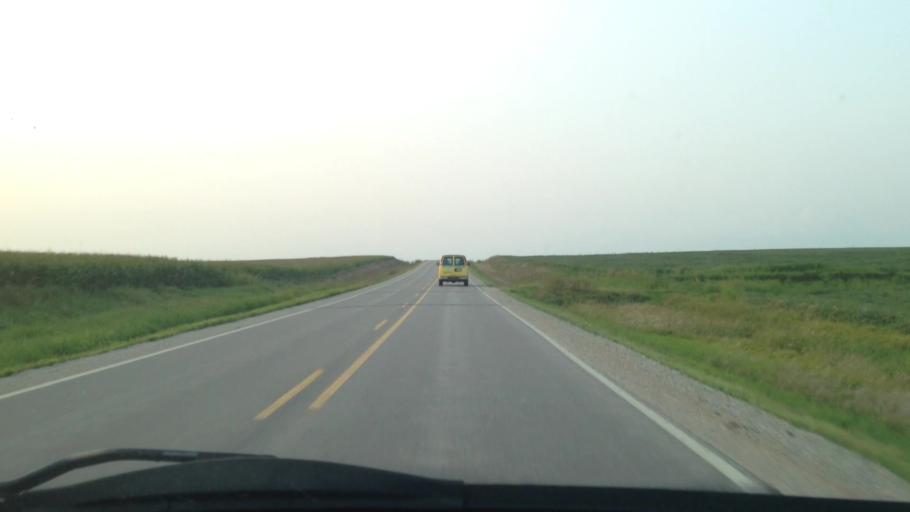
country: US
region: Iowa
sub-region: Benton County
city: Atkins
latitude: 42.0281
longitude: -91.8740
